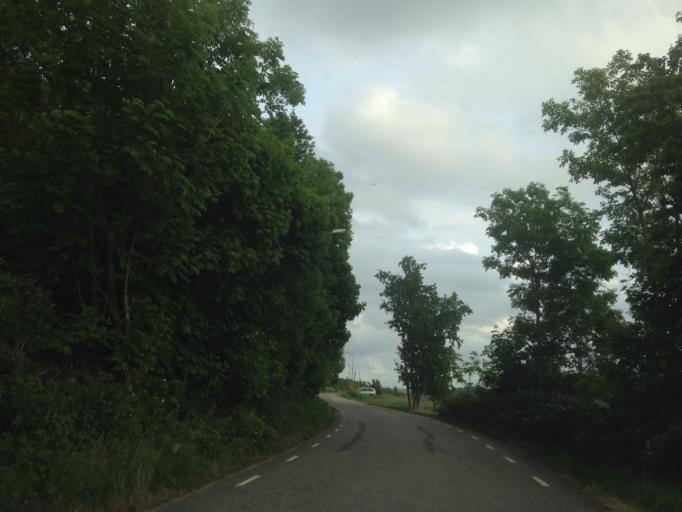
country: SE
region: Vaestra Goetaland
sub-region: Kungalvs Kommun
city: Kungalv
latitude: 57.7988
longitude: 11.9213
